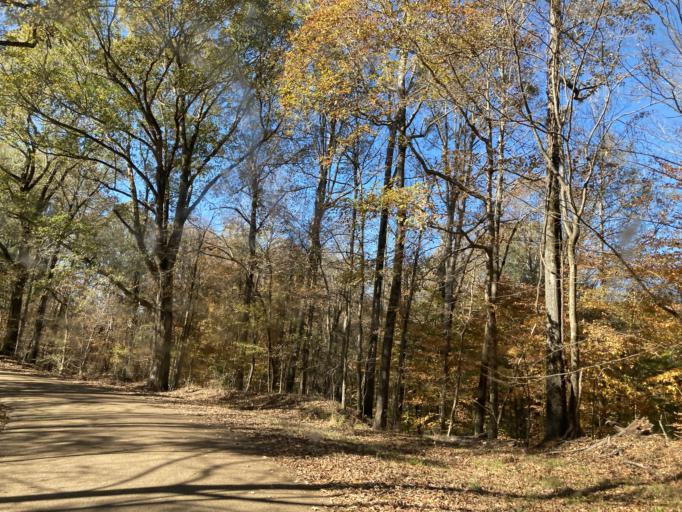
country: US
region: Mississippi
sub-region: Hinds County
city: Lynchburg
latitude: 32.5894
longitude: -90.5194
